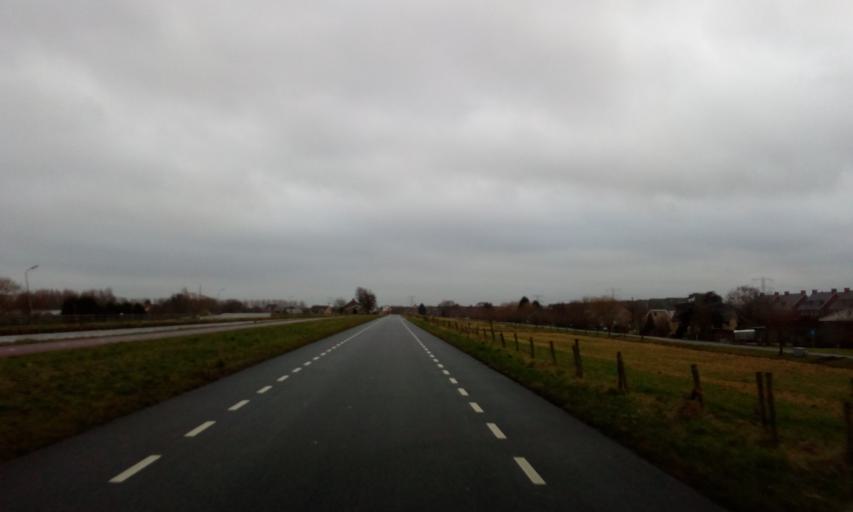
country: NL
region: South Holland
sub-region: Gemeente Capelle aan den IJssel
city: Capelle aan den IJssel
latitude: 51.9804
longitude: 4.5951
